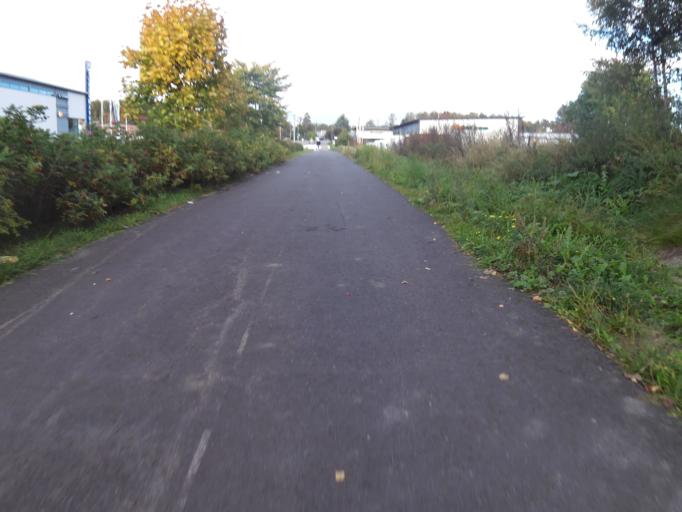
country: FI
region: Uusimaa
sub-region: Helsinki
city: Kilo
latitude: 60.2686
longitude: 24.7533
